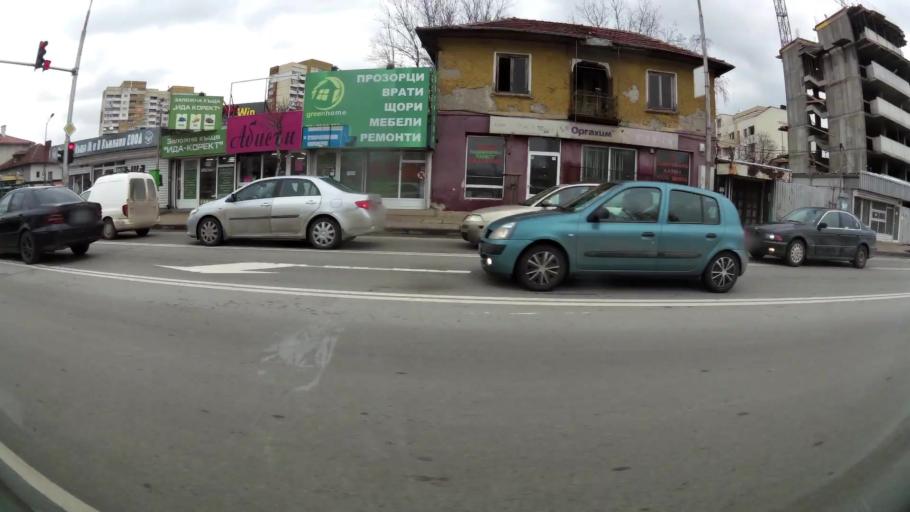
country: BG
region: Sofia-Capital
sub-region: Stolichna Obshtina
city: Sofia
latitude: 42.7320
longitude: 23.2965
